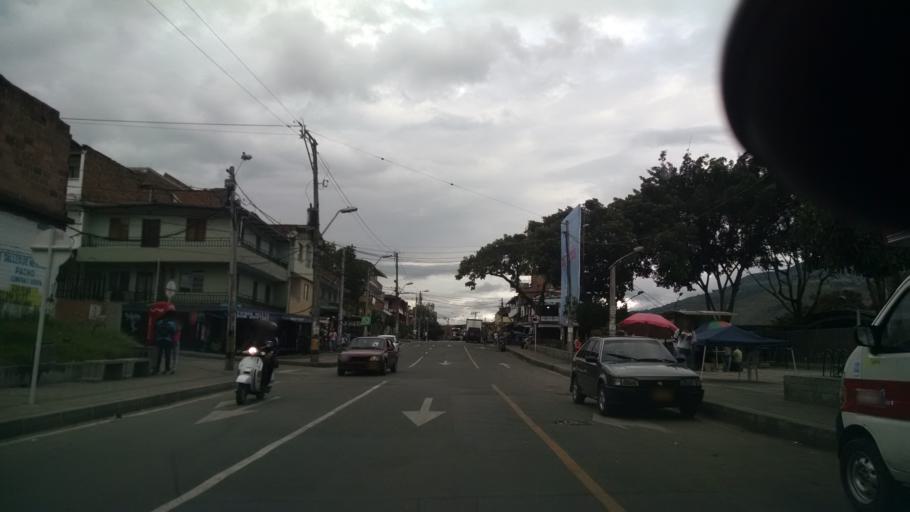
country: CO
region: Antioquia
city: Bello
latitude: 6.3025
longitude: -75.5721
